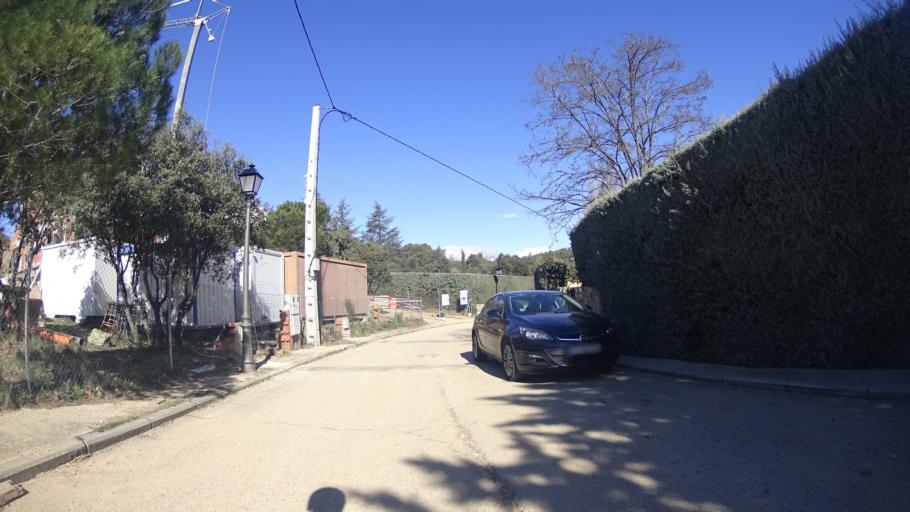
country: ES
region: Madrid
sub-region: Provincia de Madrid
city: Torrelodones
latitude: 40.5733
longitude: -3.9174
